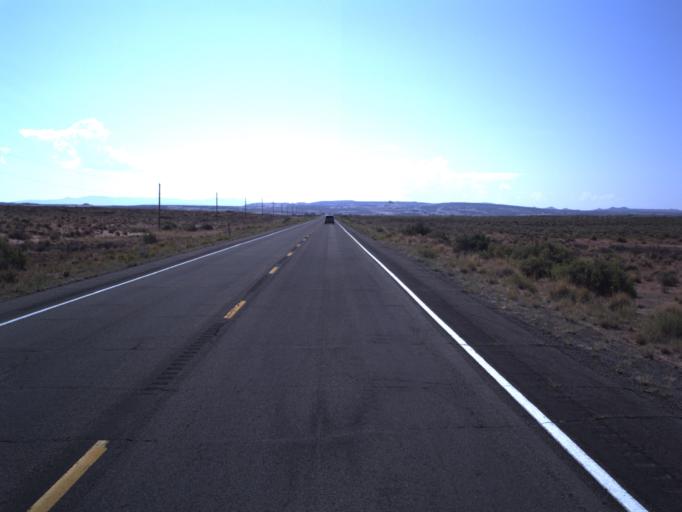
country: US
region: Utah
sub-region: San Juan County
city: Blanding
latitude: 37.1338
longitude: -109.5533
